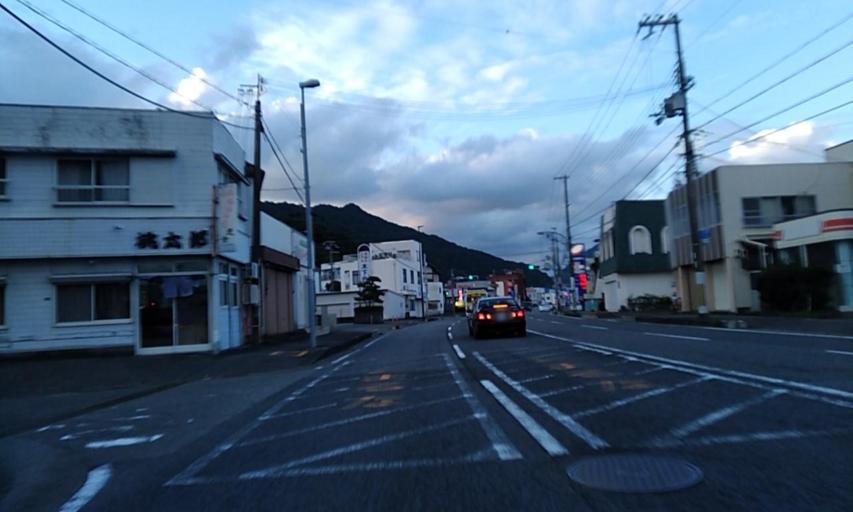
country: JP
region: Wakayama
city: Shingu
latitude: 33.7165
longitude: 135.9876
